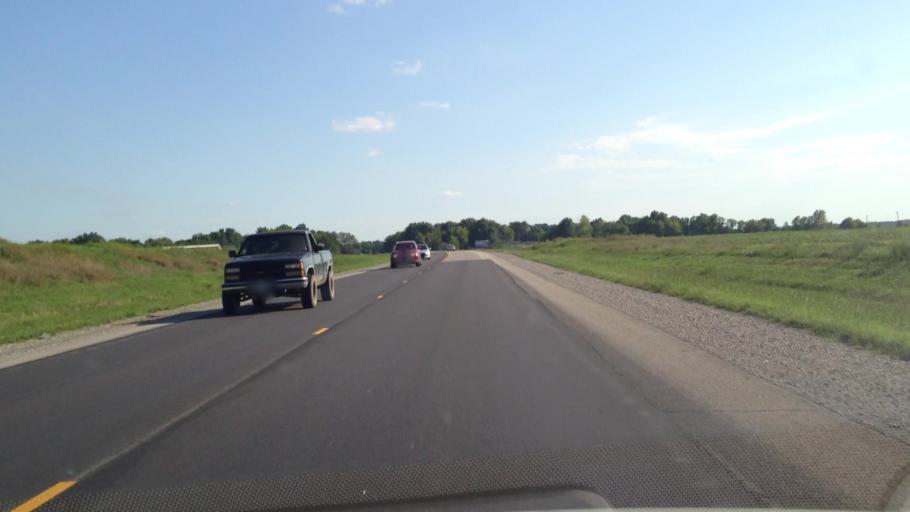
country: US
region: Kansas
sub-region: Crawford County
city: Arma
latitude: 37.5332
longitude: -94.7107
